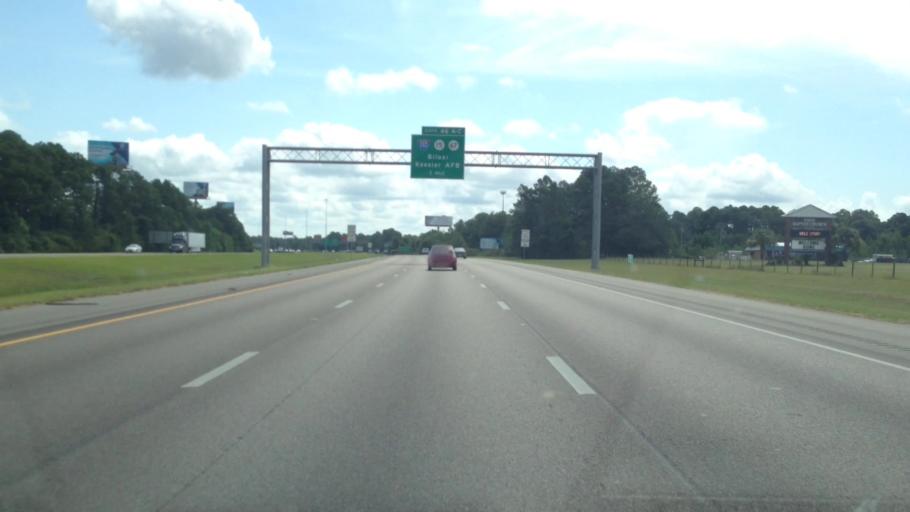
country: US
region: Mississippi
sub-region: Harrison County
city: D'Iberville
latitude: 30.4467
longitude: -88.9233
